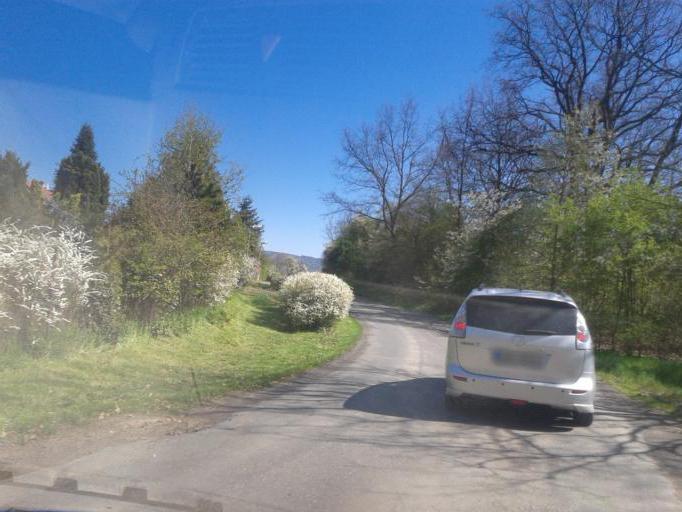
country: CZ
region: Central Bohemia
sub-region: Okres Beroun
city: Beroun
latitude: 49.8947
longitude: 14.1394
